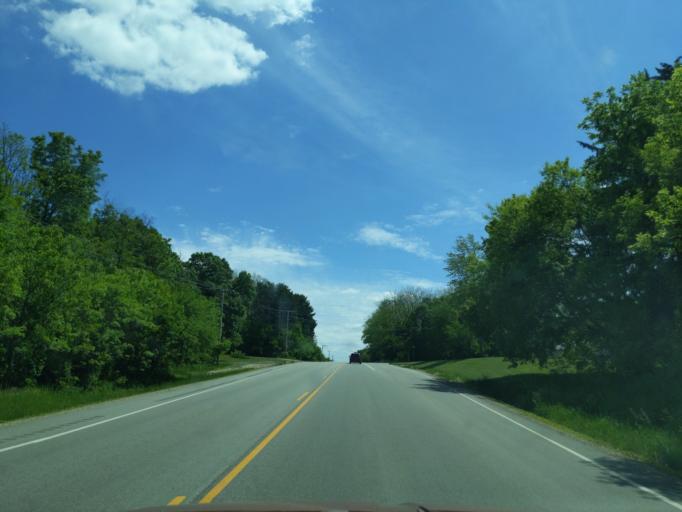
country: US
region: Wisconsin
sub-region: Columbia County
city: Pardeeville
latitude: 43.4787
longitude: -89.3152
